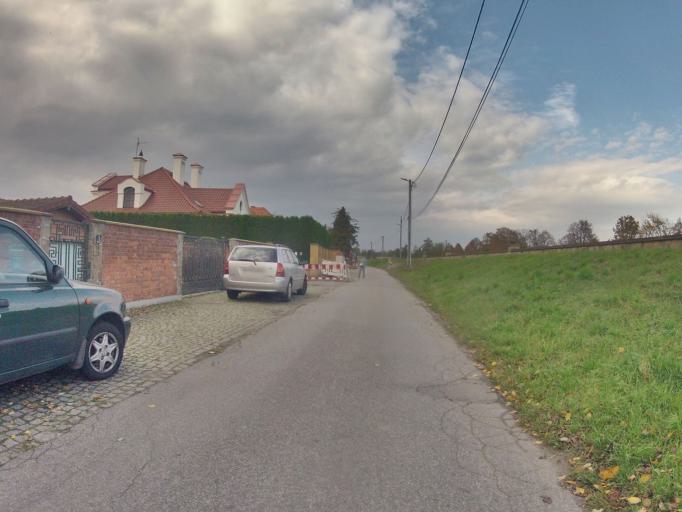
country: PL
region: Lesser Poland Voivodeship
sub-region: Krakow
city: Krakow
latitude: 50.0584
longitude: 19.9037
